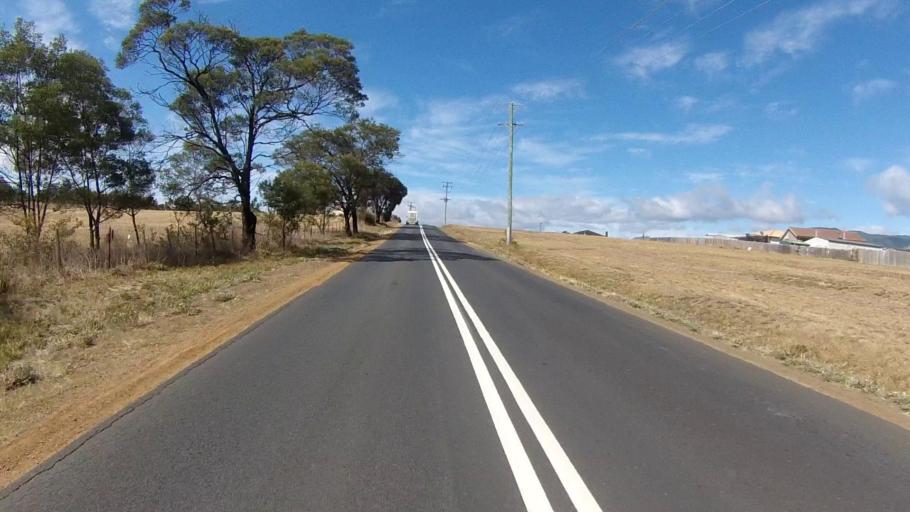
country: AU
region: Tasmania
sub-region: Brighton
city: Old Beach
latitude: -42.7472
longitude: 147.2809
